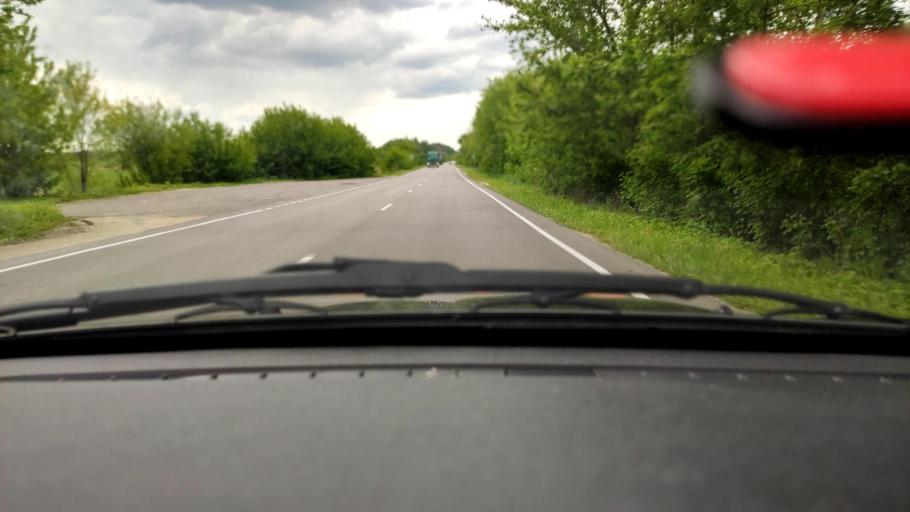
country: RU
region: Belgorod
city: Krasnoye
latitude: 51.0563
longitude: 38.8880
